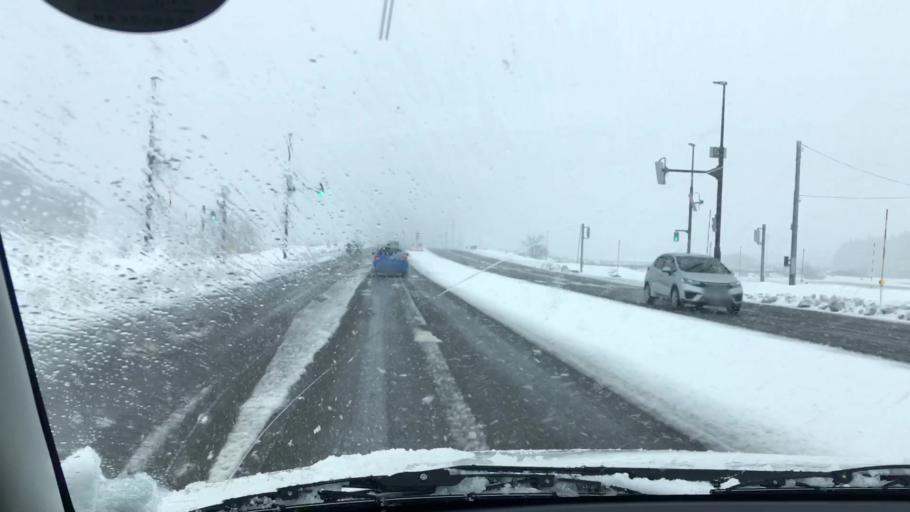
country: JP
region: Niigata
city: Joetsu
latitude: 37.0830
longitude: 138.2345
